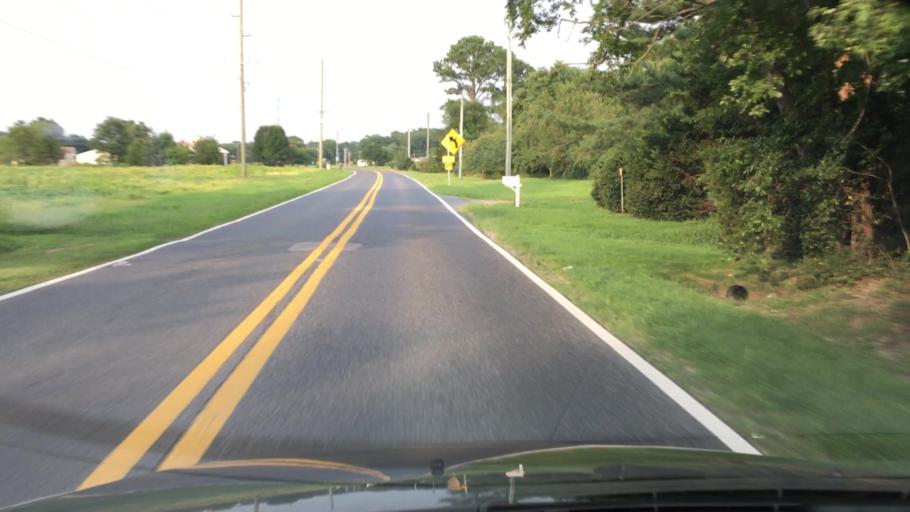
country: US
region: Delaware
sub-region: Sussex County
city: Ocean View
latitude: 38.5030
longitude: -75.1290
